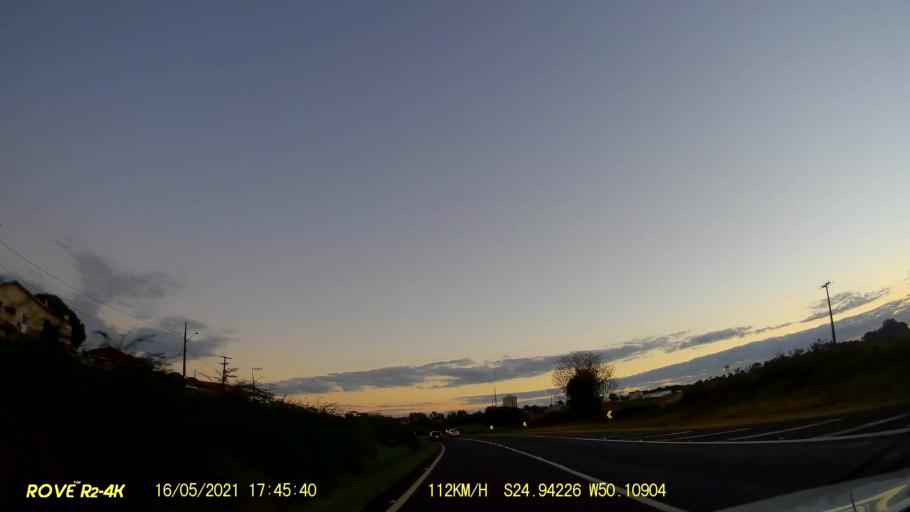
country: BR
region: Parana
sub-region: Carambei
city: Carambei
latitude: -24.9435
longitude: -50.1097
